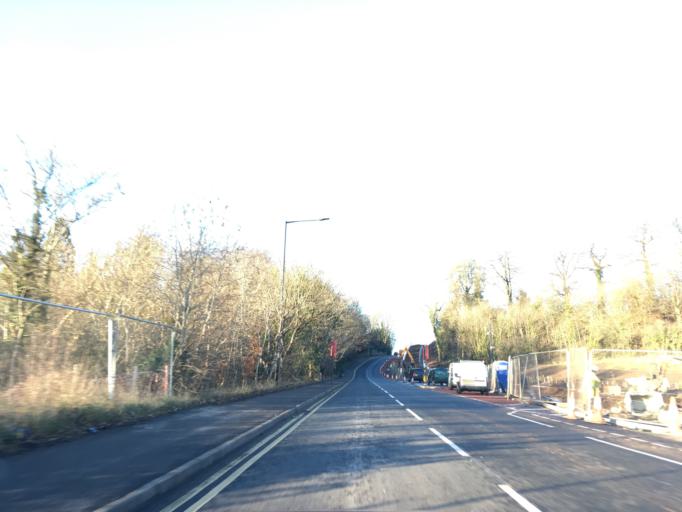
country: GB
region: England
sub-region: South Gloucestershire
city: Stoke Gifford
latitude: 51.4927
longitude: -2.5419
